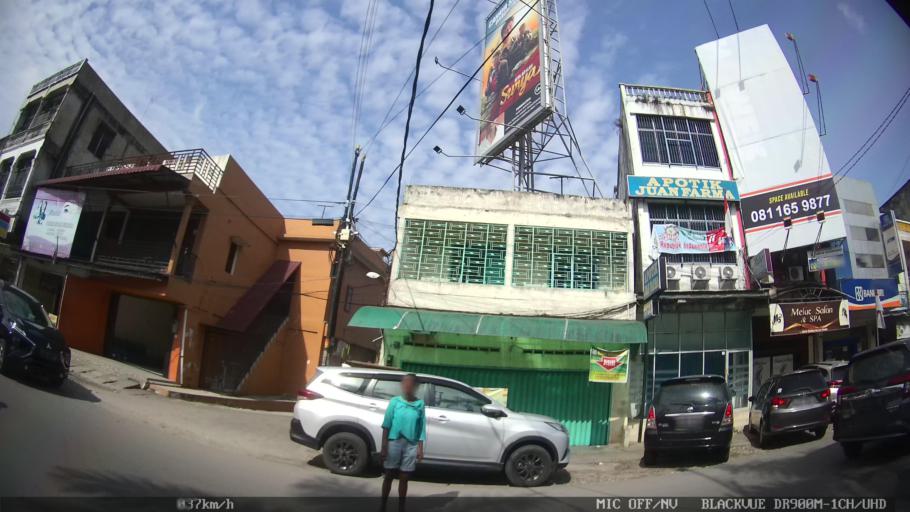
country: ID
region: North Sumatra
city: Medan
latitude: 3.5684
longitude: 98.6600
